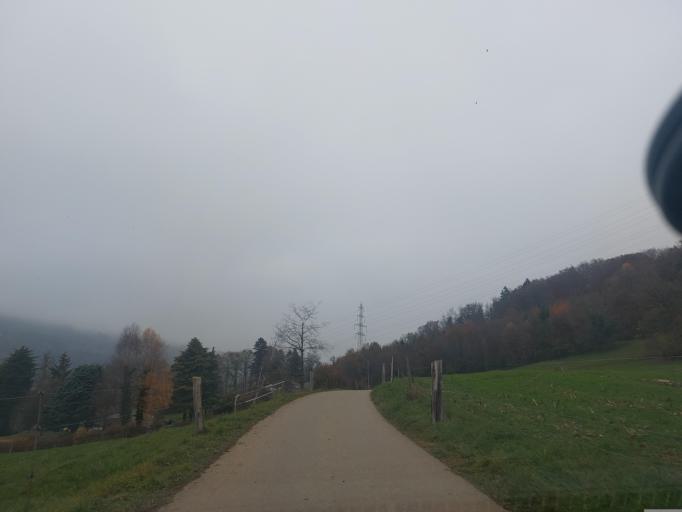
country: CH
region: Vaud
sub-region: Riviera-Pays-d'Enhaut District
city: Blonay
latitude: 46.4854
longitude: 6.8840
